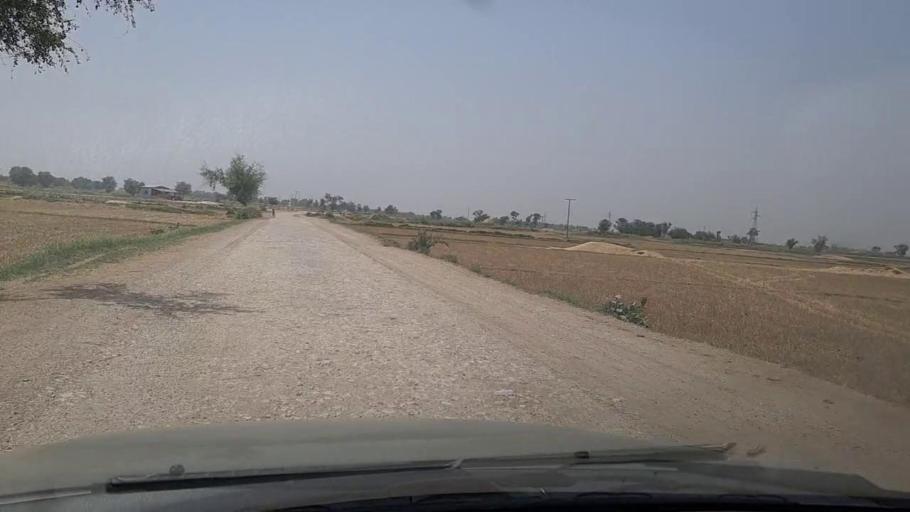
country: PK
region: Sindh
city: Miro Khan
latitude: 27.7767
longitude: 68.1746
